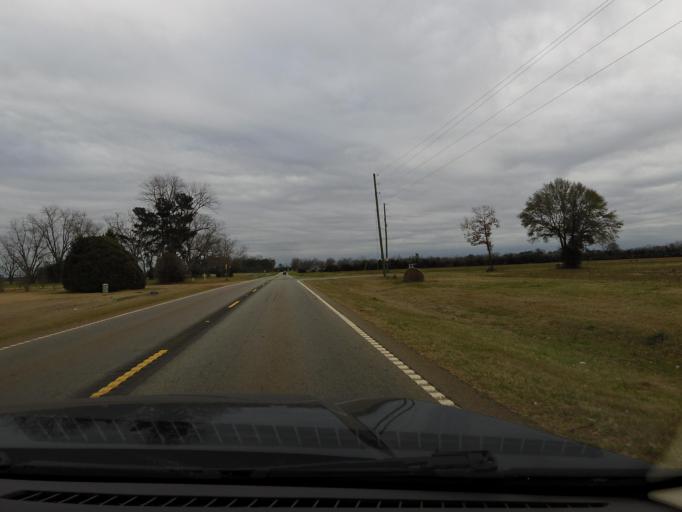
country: US
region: Georgia
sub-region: Randolph County
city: Shellman
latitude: 31.7721
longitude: -84.6236
